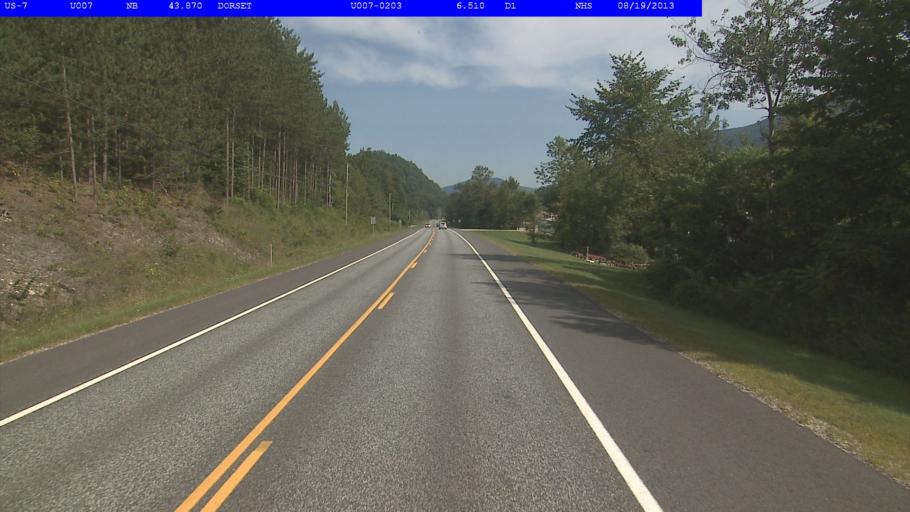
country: US
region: Vermont
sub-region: Bennington County
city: Manchester Center
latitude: 43.3020
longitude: -72.9955
